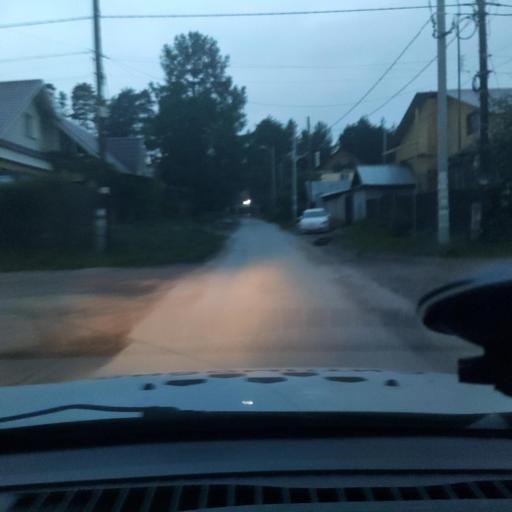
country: RU
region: Perm
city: Kondratovo
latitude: 58.0316
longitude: 56.0050
